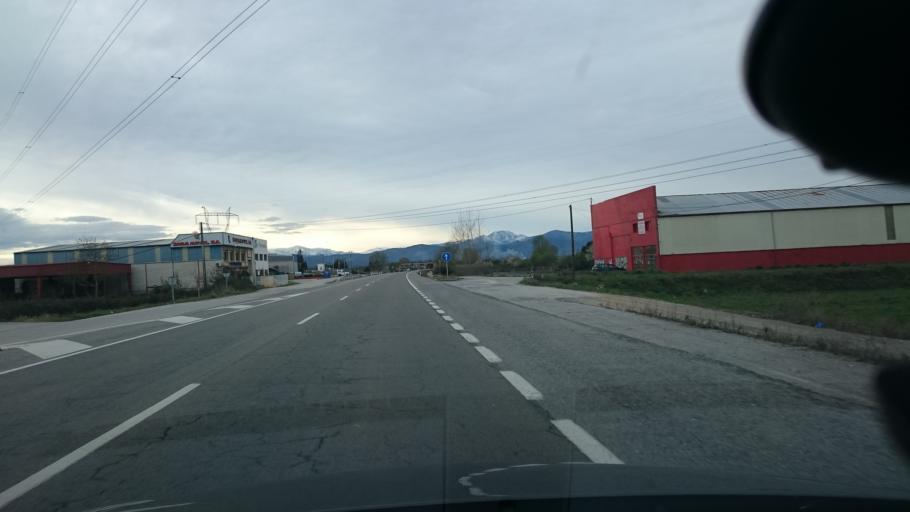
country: ES
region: Castille and Leon
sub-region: Provincia de Leon
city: Camponaraya
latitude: 42.5657
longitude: -6.6665
